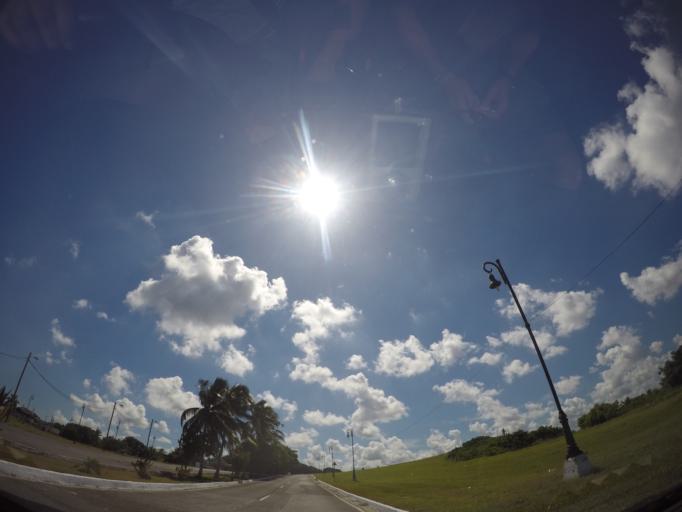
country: CU
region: La Habana
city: Centro Habana
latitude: 23.1498
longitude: -82.3528
